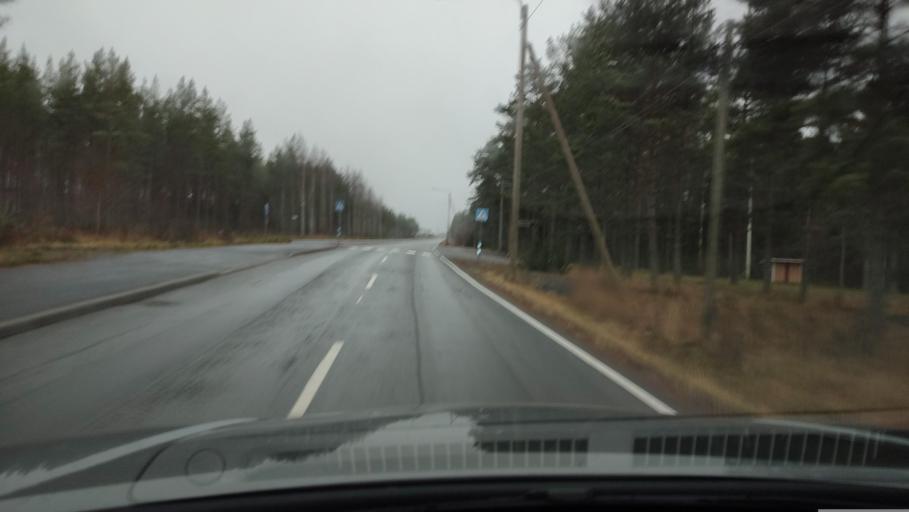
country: FI
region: Ostrobothnia
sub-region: Sydosterbotten
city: Kristinestad
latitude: 62.2361
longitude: 21.5208
